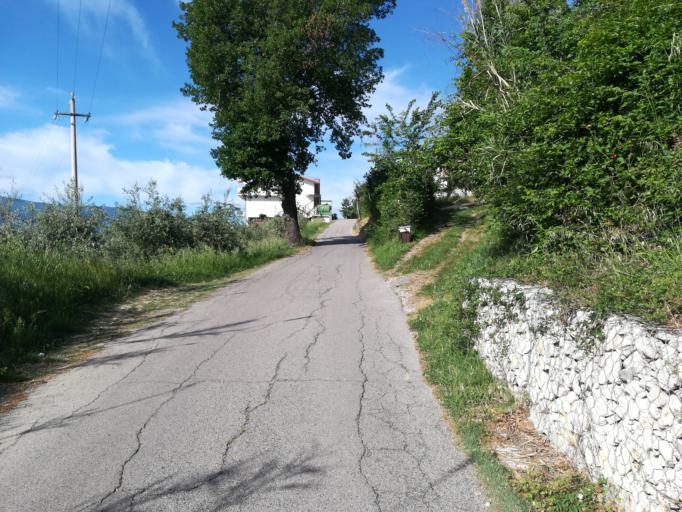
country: IT
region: Abruzzo
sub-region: Provincia di Chieti
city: Bucchianico
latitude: 42.2963
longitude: 14.1714
